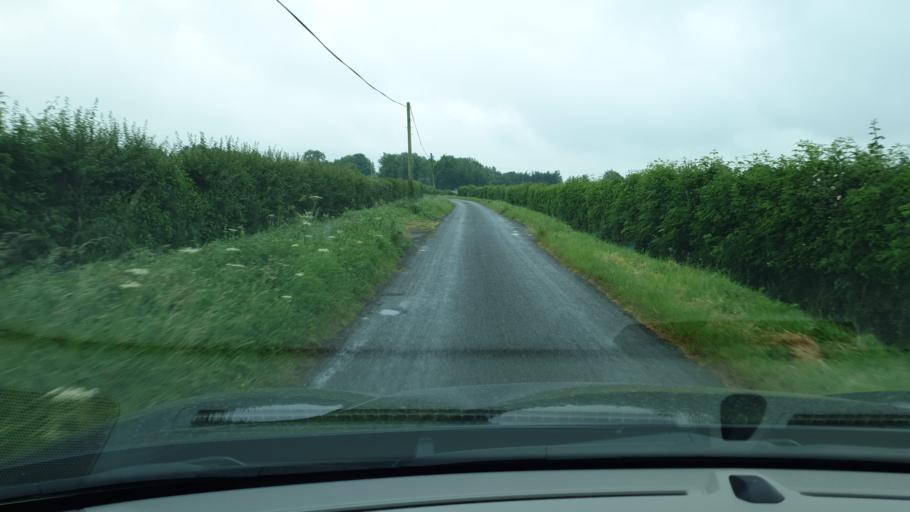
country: IE
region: Leinster
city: Hartstown
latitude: 53.4403
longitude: -6.4299
